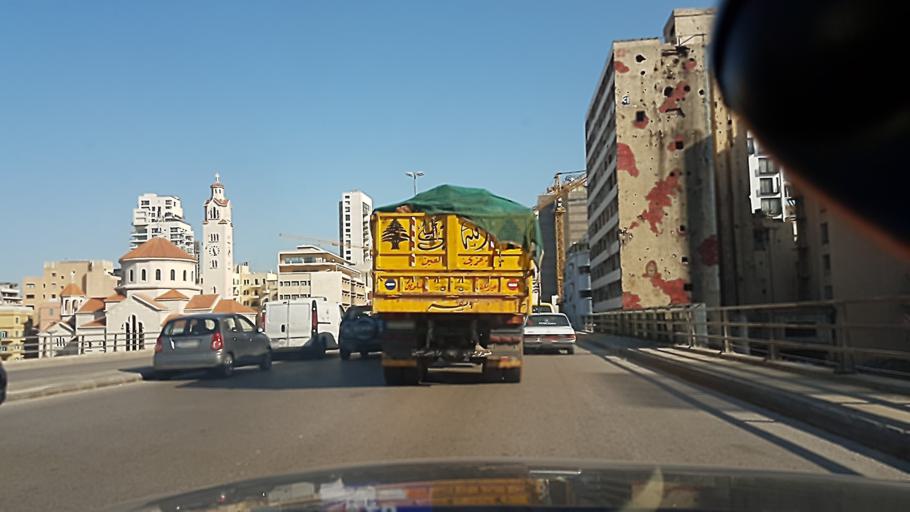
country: LB
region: Beyrouth
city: Beirut
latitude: 33.8922
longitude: 35.5063
